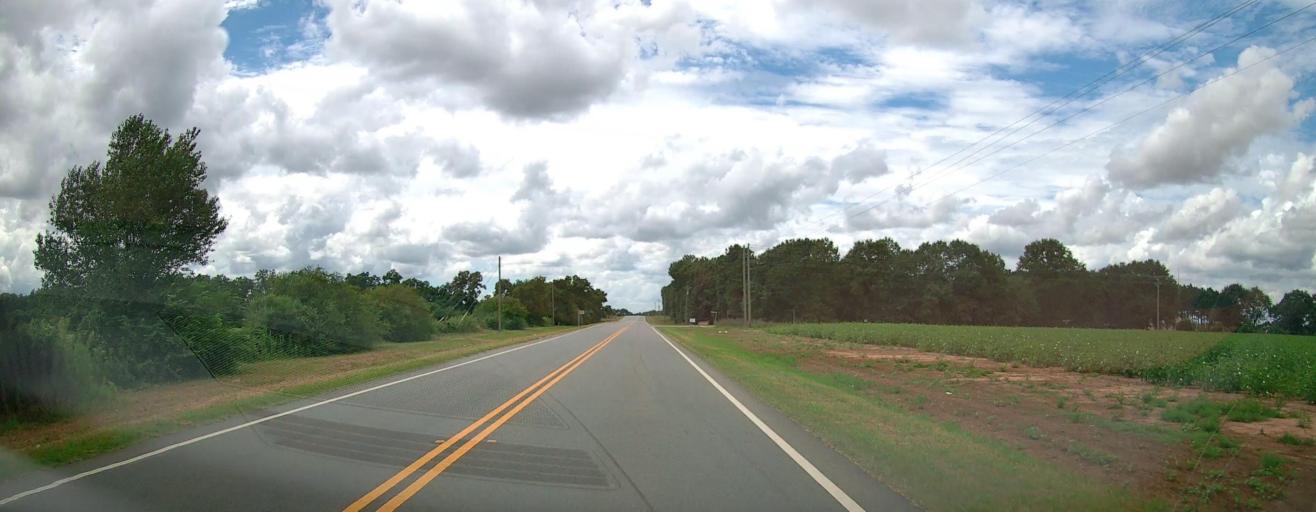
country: US
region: Georgia
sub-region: Macon County
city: Montezuma
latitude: 32.2916
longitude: -83.9237
